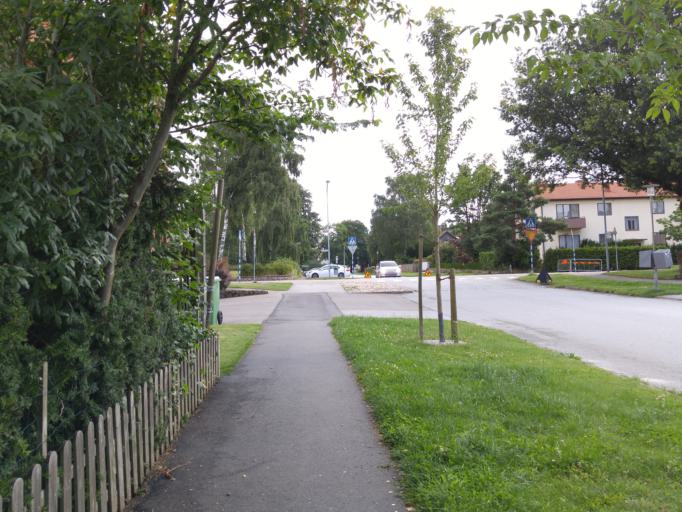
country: SE
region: Skane
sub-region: Hoors Kommun
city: Hoeoer
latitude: 55.9311
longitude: 13.5415
